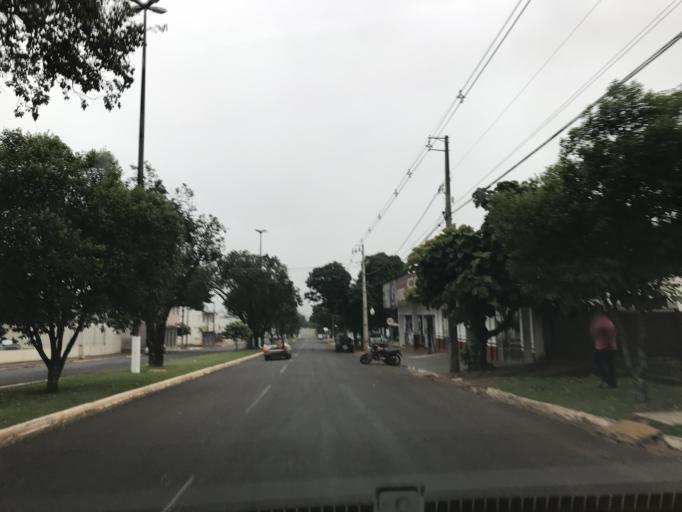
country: PY
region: Canindeyu
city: Salto del Guaira
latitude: -24.1581
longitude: -54.0998
